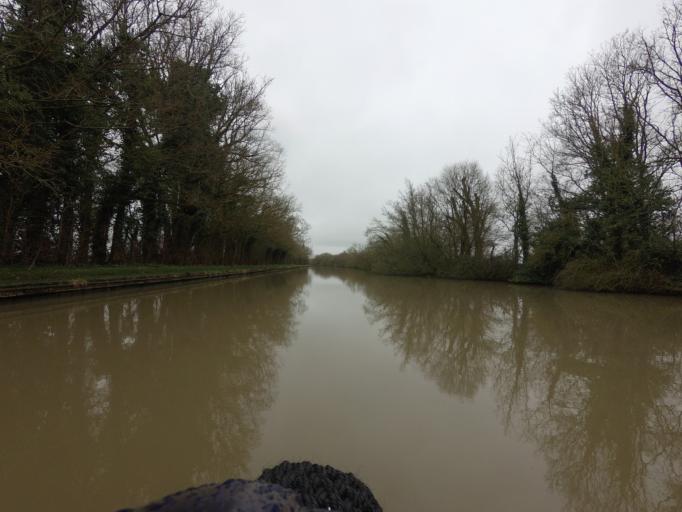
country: GB
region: England
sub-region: Milton Keynes
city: Castlethorpe
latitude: 52.0876
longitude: -0.8596
